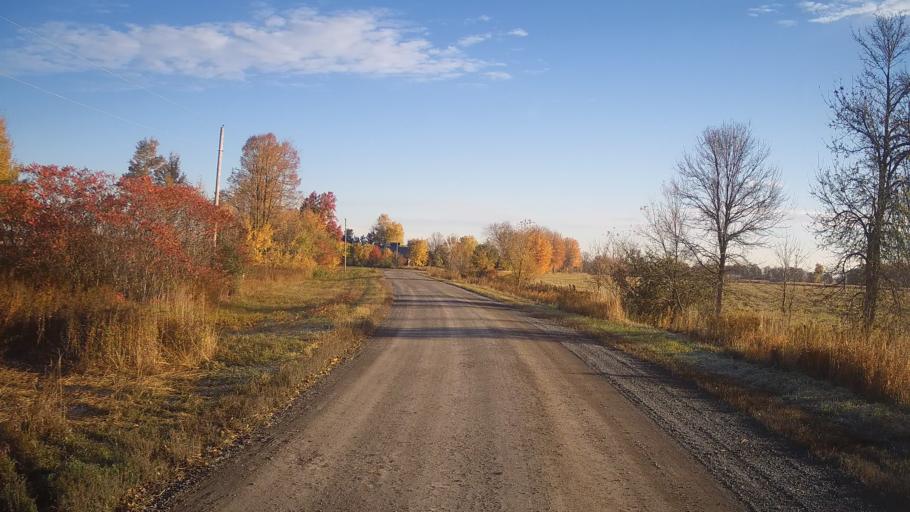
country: CA
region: Ontario
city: Arnprior
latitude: 45.3510
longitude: -76.3114
